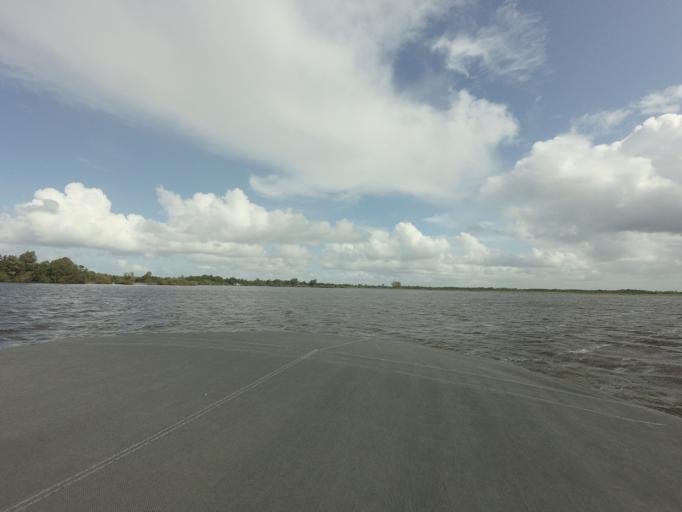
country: NL
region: Friesland
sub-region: Gemeente Boarnsterhim
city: Warten
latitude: 53.1135
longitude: 5.9282
